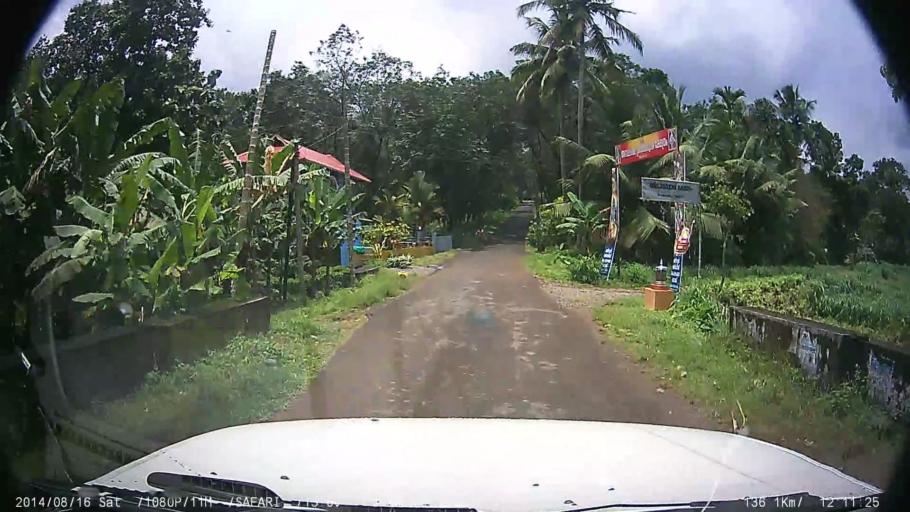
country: IN
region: Kerala
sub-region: Kottayam
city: Palackattumala
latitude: 9.7869
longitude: 76.5578
